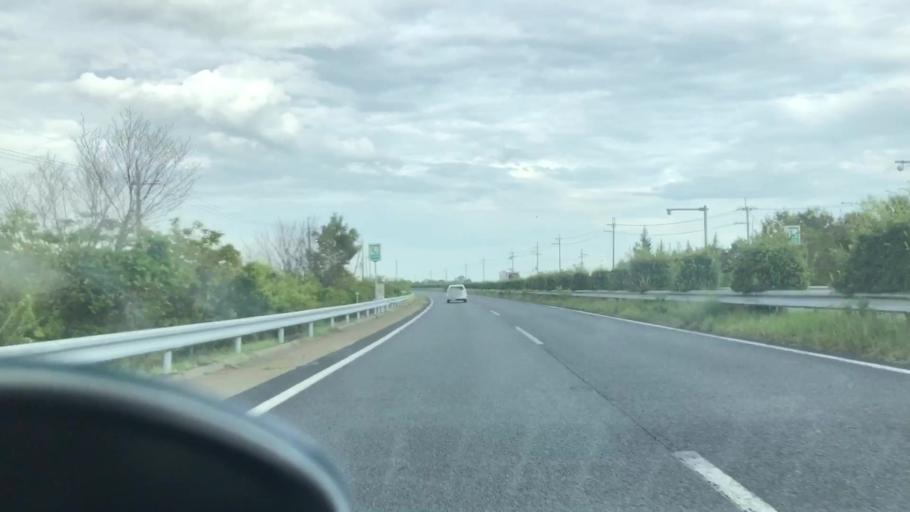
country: JP
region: Hyogo
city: Yashiro
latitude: 34.9291
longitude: 134.8994
